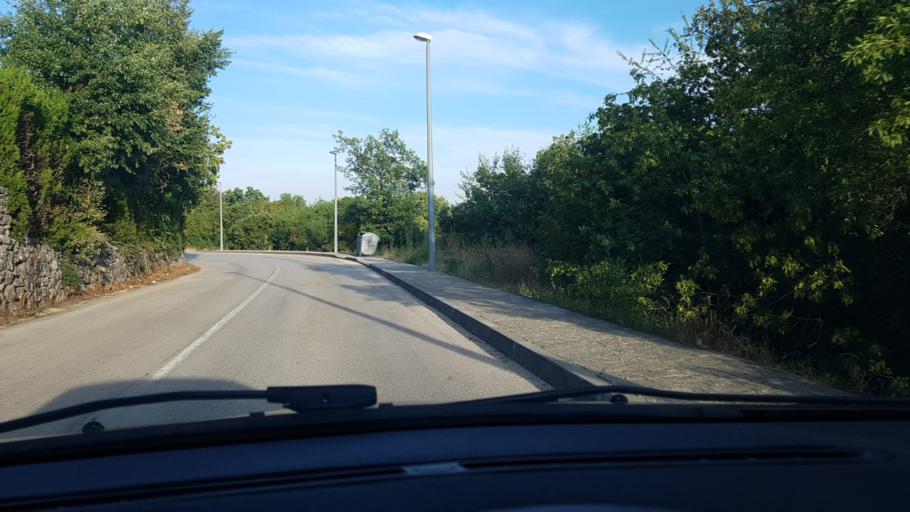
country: HR
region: Splitsko-Dalmatinska
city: Imotski
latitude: 43.4448
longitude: 17.2031
